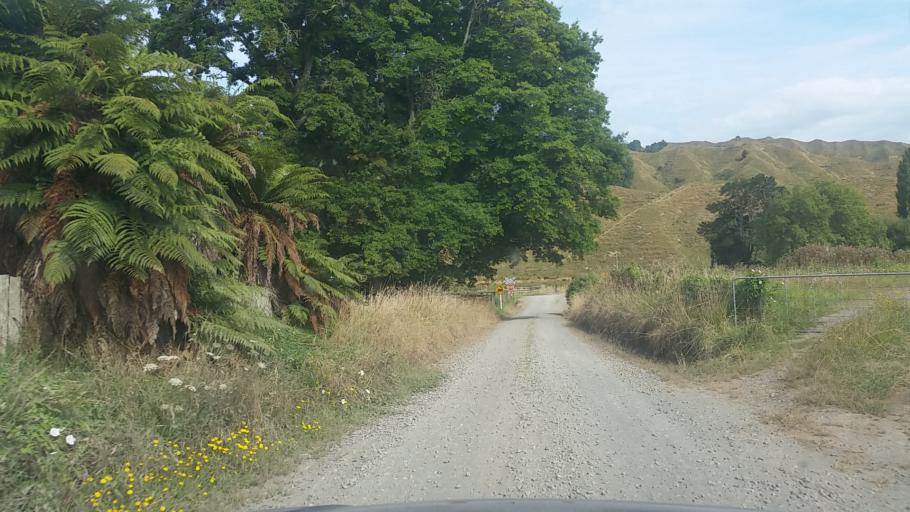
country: NZ
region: Taranaki
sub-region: New Plymouth District
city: Waitara
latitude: -39.1078
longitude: 174.7490
